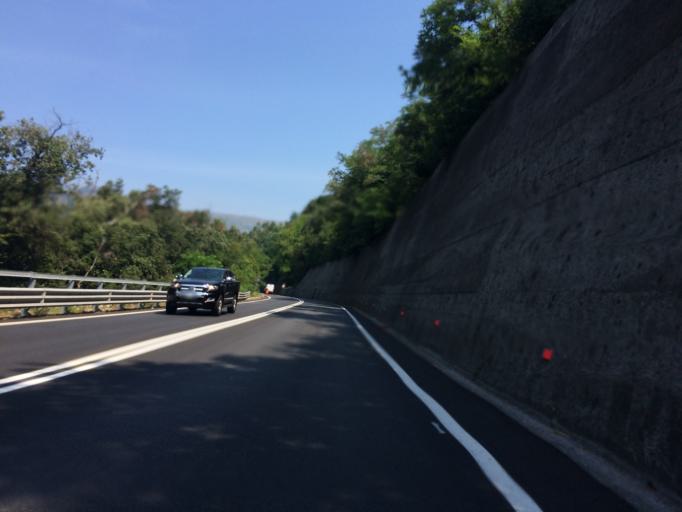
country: IT
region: Liguria
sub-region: Provincia di Genova
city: Cogoleto
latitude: 44.3935
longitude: 8.6651
